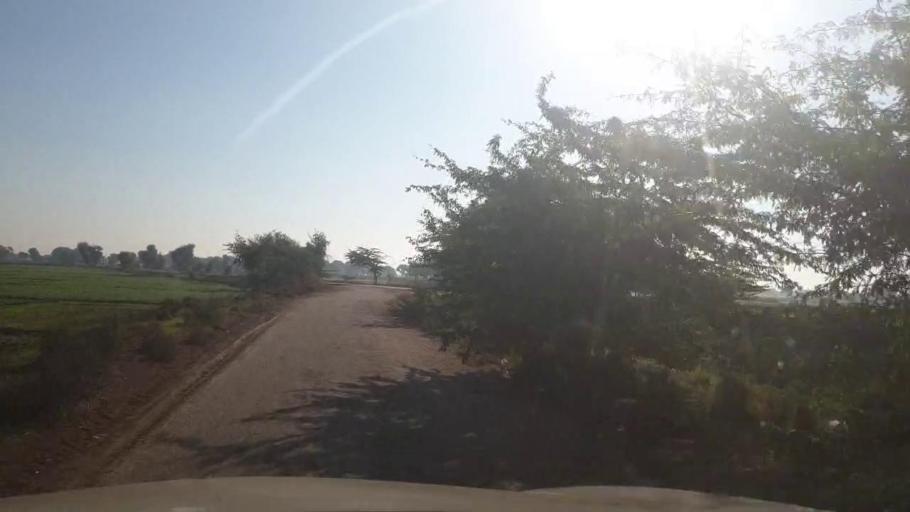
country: PK
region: Sindh
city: Bhan
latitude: 26.5414
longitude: 67.6856
